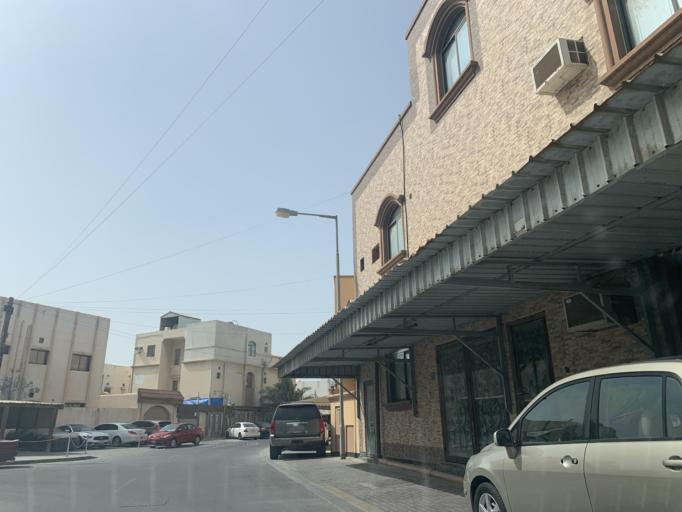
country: BH
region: Northern
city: Madinat `Isa
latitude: 26.1801
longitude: 50.5260
